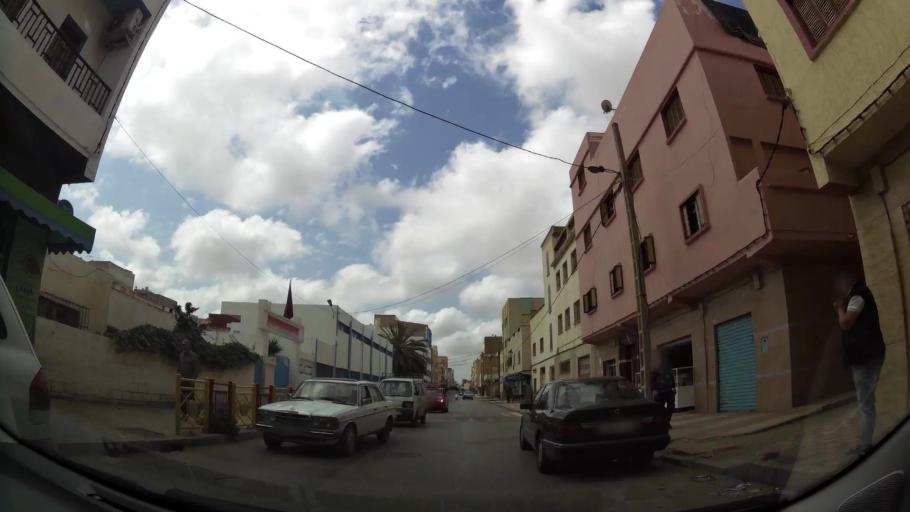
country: MA
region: Oriental
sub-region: Nador
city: Nador
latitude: 35.1681
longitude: -2.9307
